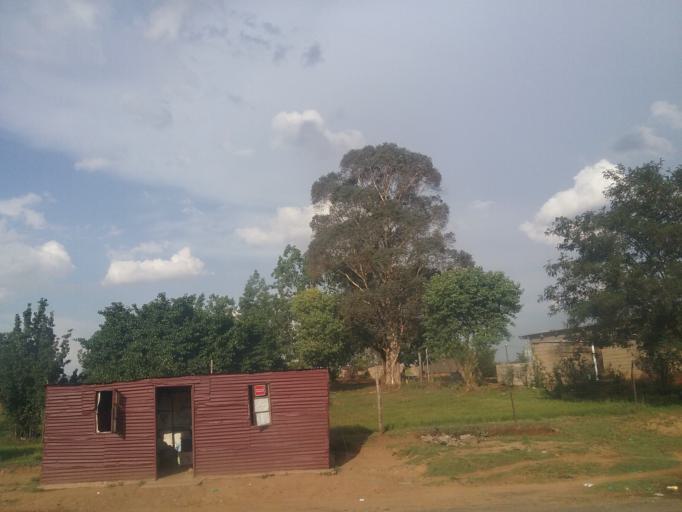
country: LS
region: Leribe
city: Leribe
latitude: -28.9260
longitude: 28.1307
